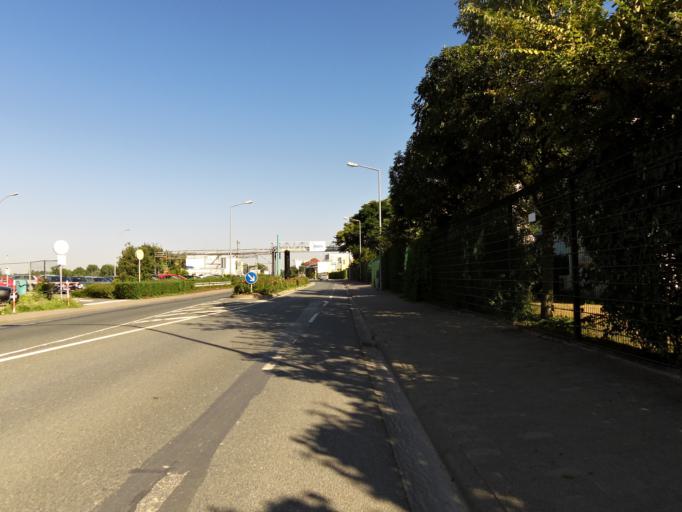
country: DE
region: Hesse
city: Gernsheim
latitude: 49.7672
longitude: 8.4797
